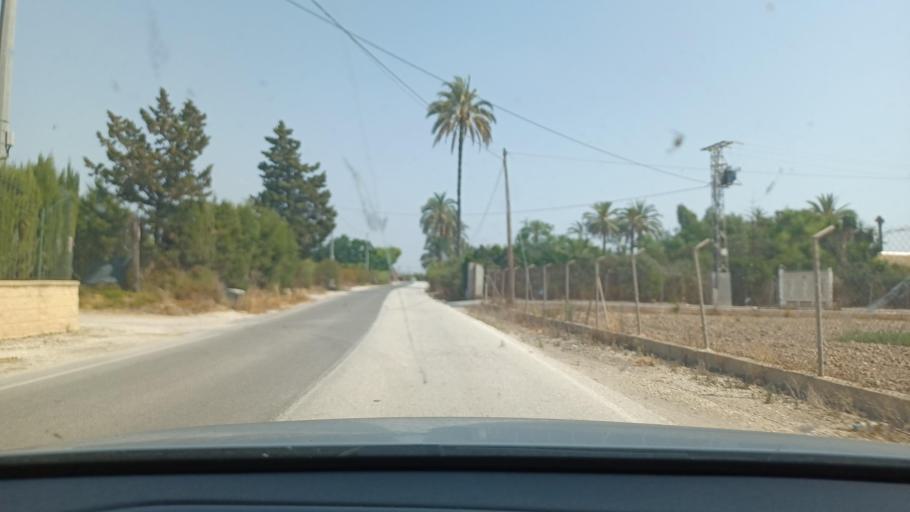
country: ES
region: Valencia
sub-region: Provincia de Alicante
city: Elche
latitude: 38.2365
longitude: -0.6927
